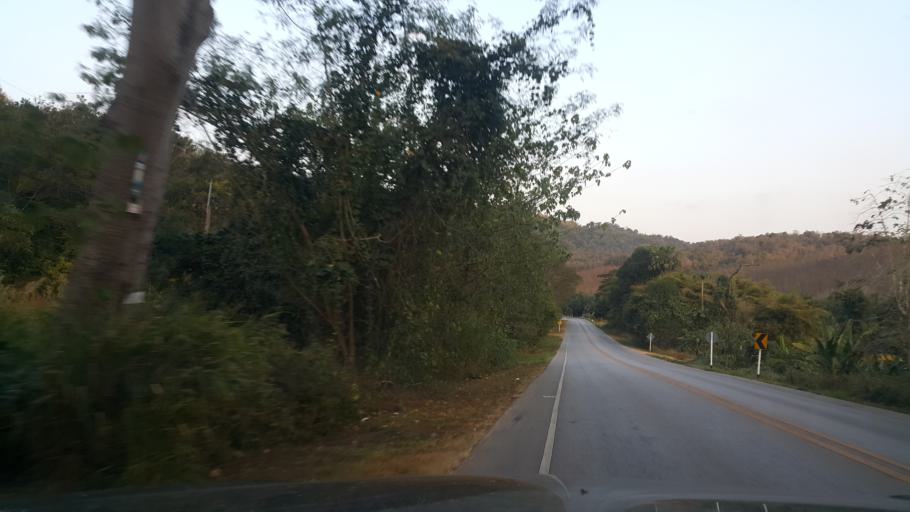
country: TH
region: Loei
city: Loei
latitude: 17.4668
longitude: 101.5907
